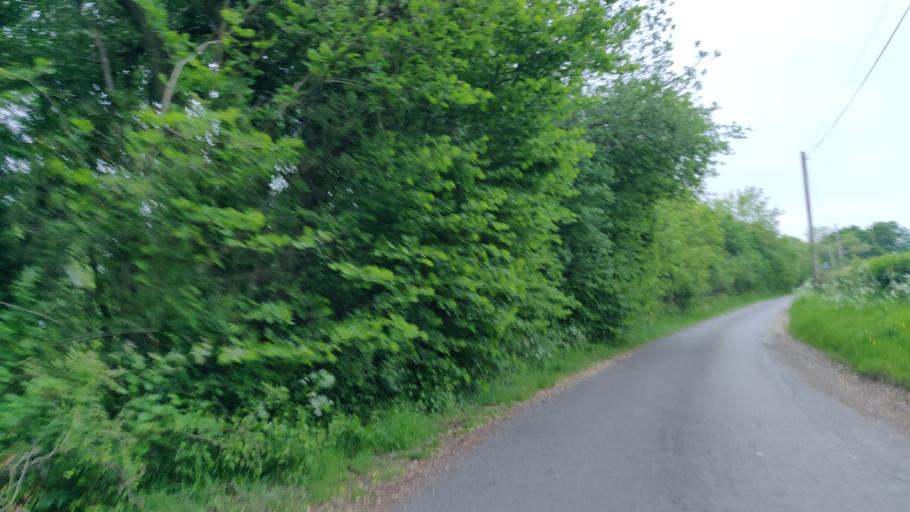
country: GB
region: England
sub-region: West Sussex
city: Southwater
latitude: 51.0284
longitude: -0.3346
